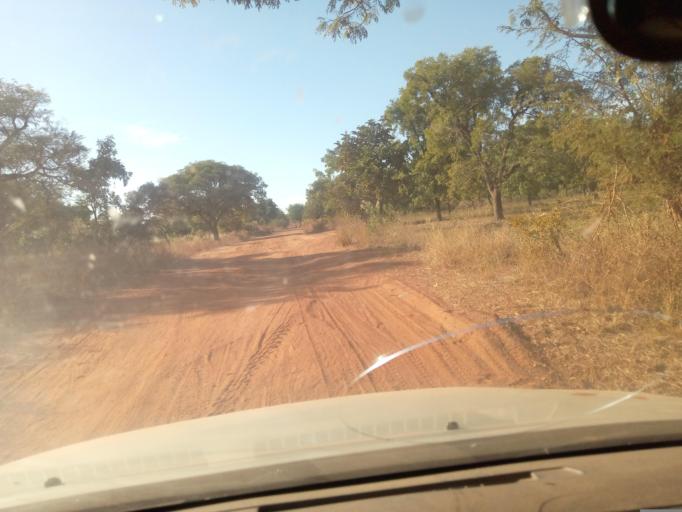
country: ML
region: Sikasso
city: Sikasso
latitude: 11.4719
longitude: -5.4588
